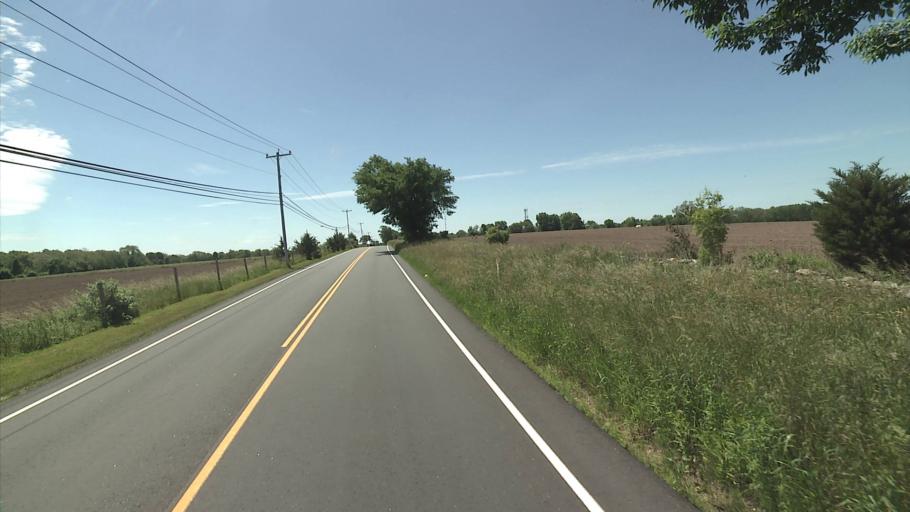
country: US
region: Connecticut
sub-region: Windham County
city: Moosup
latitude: 41.6706
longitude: -71.8488
